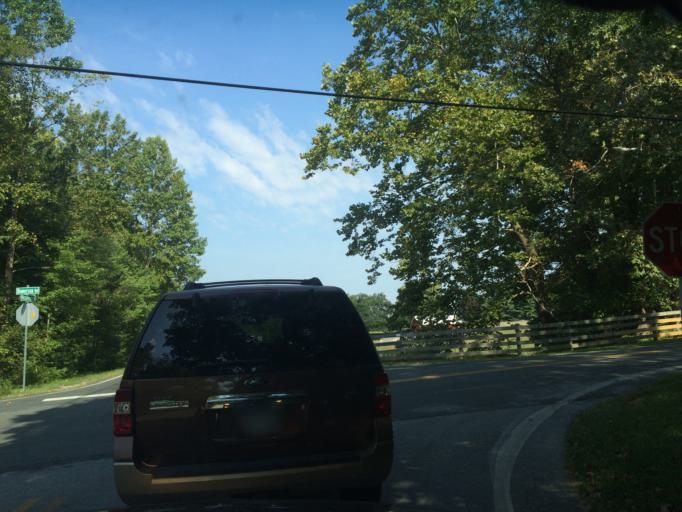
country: US
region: Maryland
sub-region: Carroll County
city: New Windsor
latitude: 39.5273
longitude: -77.0549
